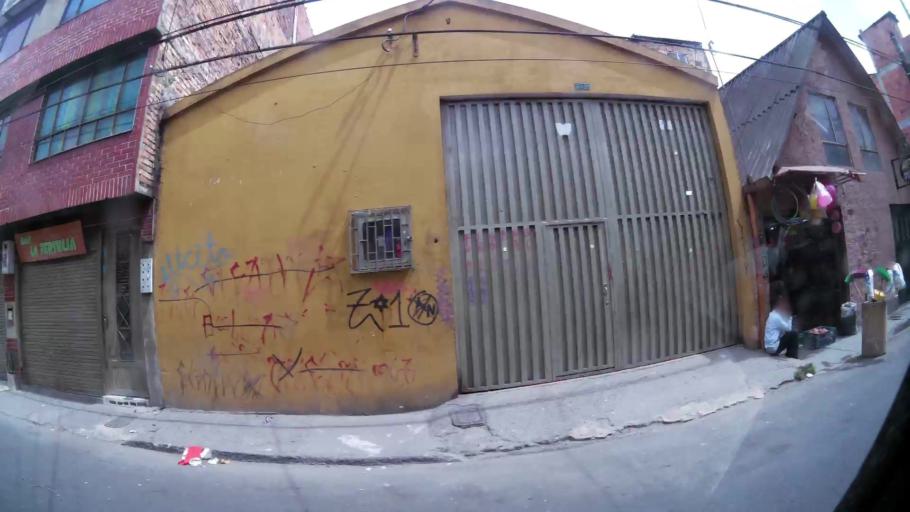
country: CO
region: Cundinamarca
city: Funza
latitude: 4.7137
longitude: -74.1421
